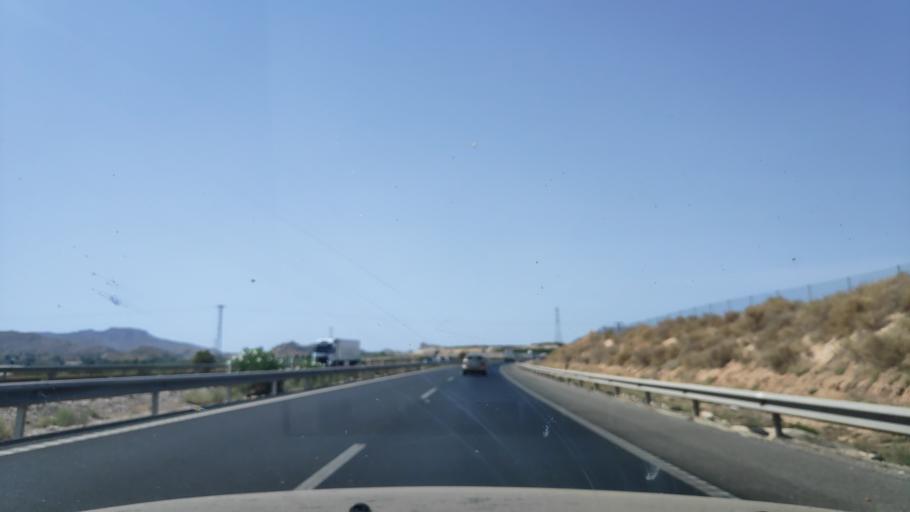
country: ES
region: Murcia
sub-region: Murcia
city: Archena
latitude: 38.1387
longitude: -1.2722
